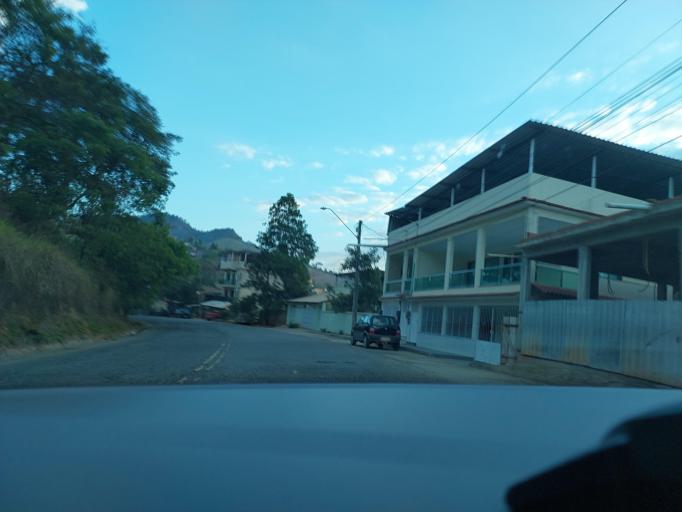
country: BR
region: Rio de Janeiro
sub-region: Natividade
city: Natividade
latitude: -21.2007
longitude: -42.1238
